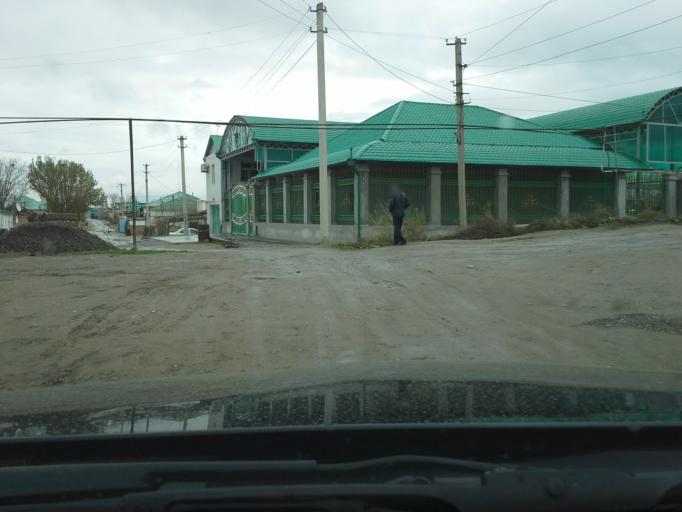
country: TM
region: Ahal
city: Abadan
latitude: 37.9622
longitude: 58.2080
